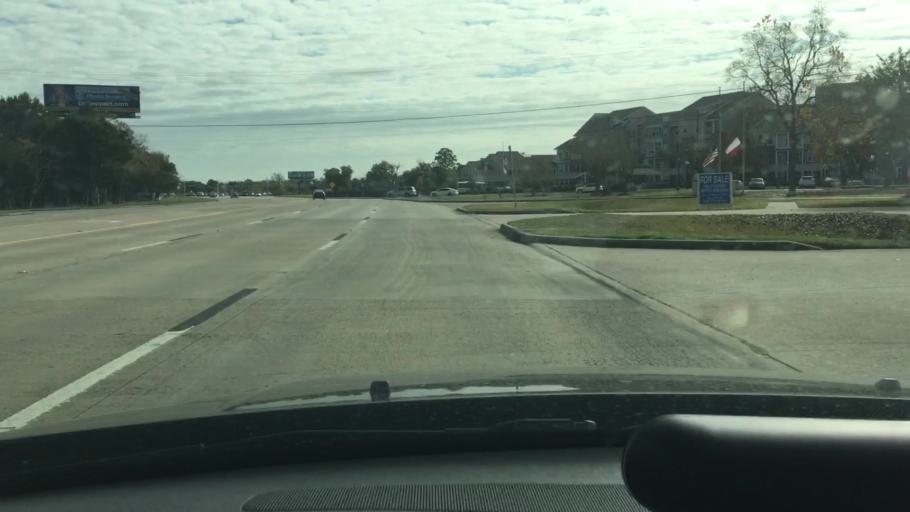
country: US
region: Texas
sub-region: Galveston County
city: League City
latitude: 29.5234
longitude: -95.0832
